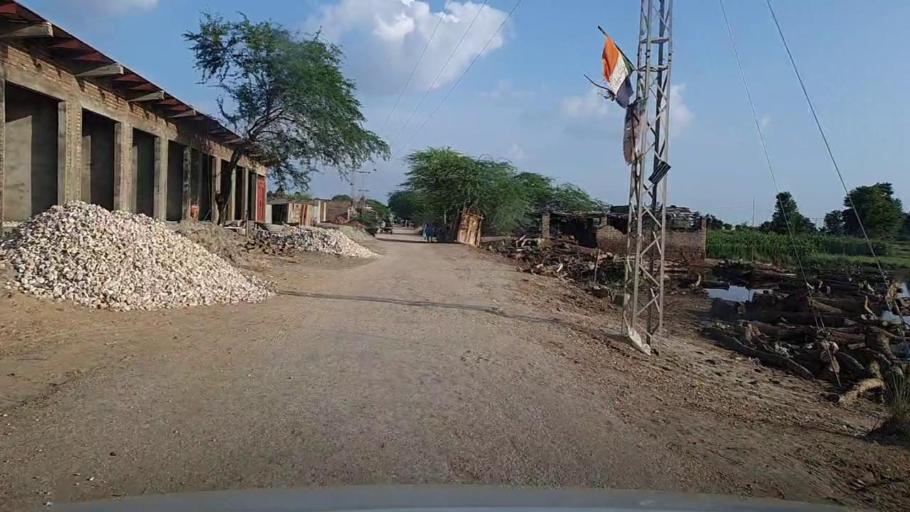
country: PK
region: Sindh
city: Hingorja
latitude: 27.0917
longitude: 68.4170
